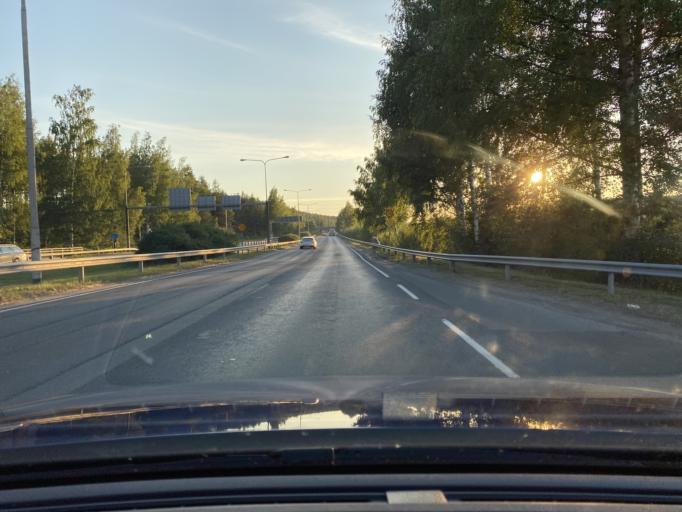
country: FI
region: Pirkanmaa
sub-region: Tampere
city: Pirkkala
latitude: 61.5106
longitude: 23.6868
